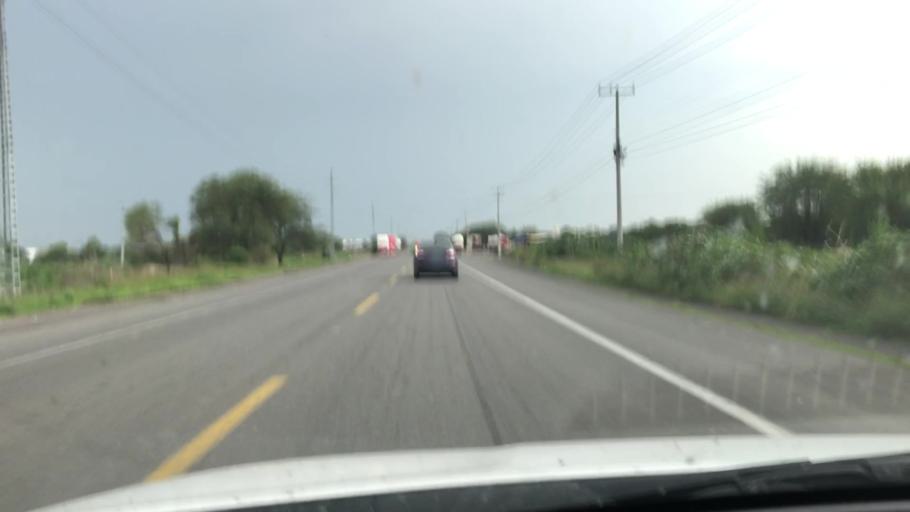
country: MX
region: Michoacan
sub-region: Vista Hermosa
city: Los Pilares
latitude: 20.2745
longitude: -102.4032
